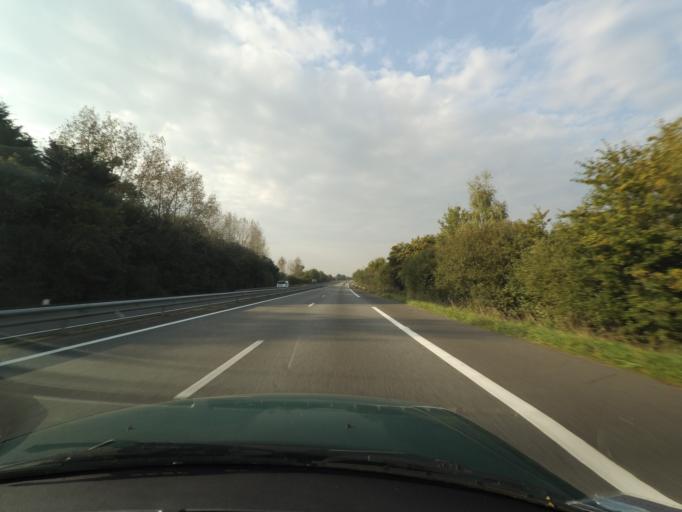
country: FR
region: Pays de la Loire
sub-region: Departement de la Loire-Atlantique
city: Derval
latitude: 47.6599
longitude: -1.6780
